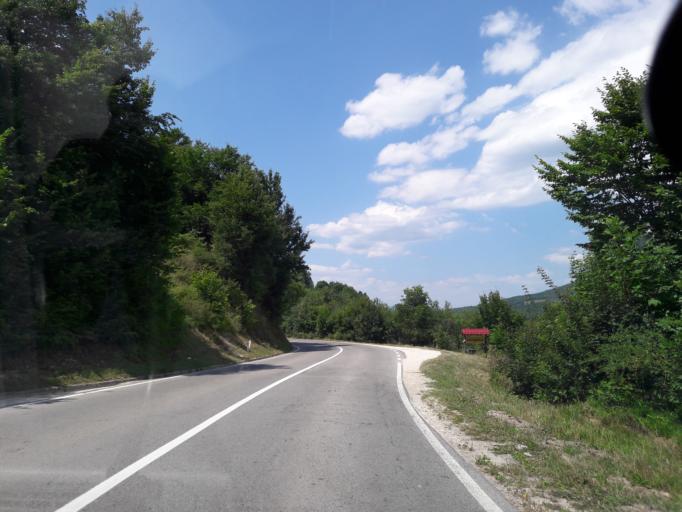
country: BA
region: Republika Srpska
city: Sipovo
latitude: 44.2056
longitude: 17.1370
